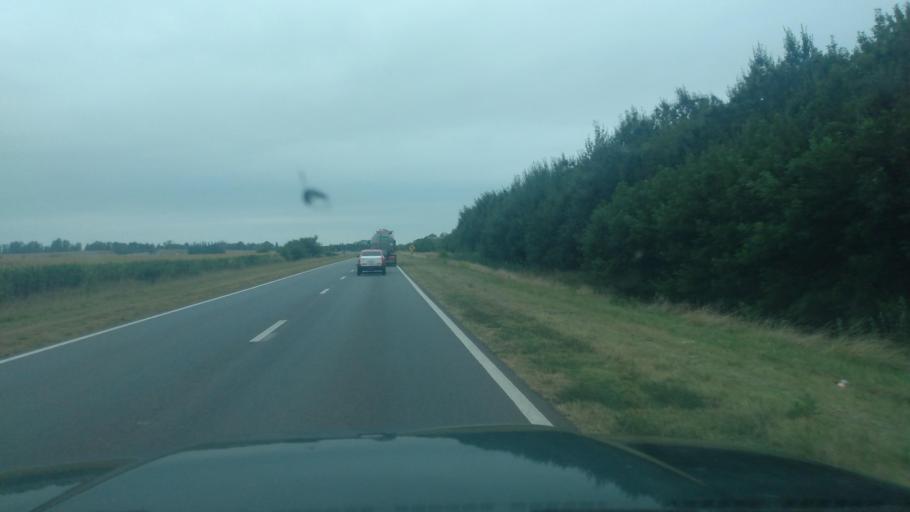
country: AR
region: Buenos Aires
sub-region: Partido de Alberti
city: Alberti
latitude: -35.0143
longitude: -60.1197
